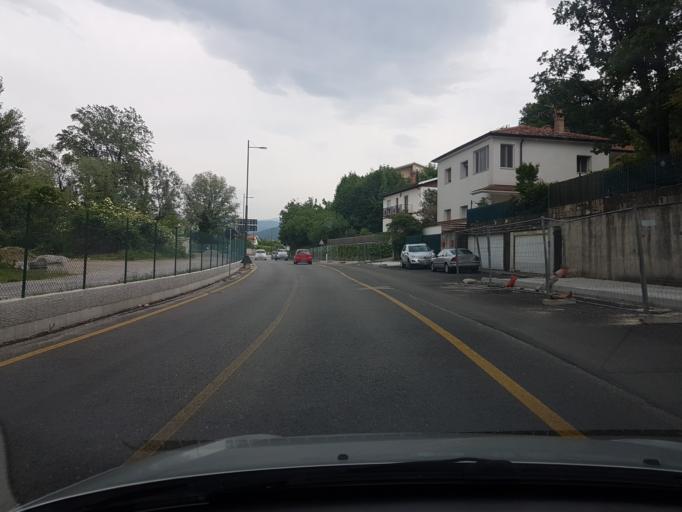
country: IT
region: Friuli Venezia Giulia
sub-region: Provincia di Trieste
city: Muggia
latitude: 45.5961
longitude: 13.7859
